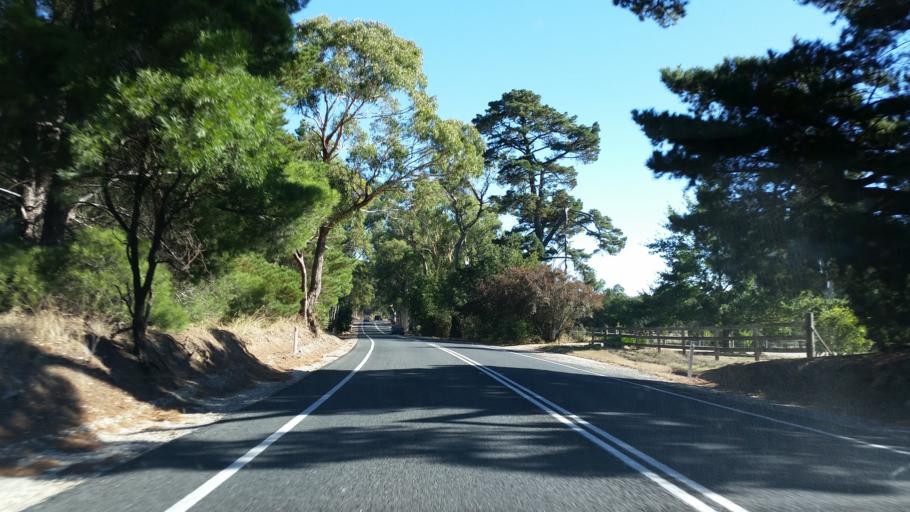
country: AU
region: South Australia
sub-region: Adelaide Hills
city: Birdwood
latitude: -34.8076
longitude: 138.9805
